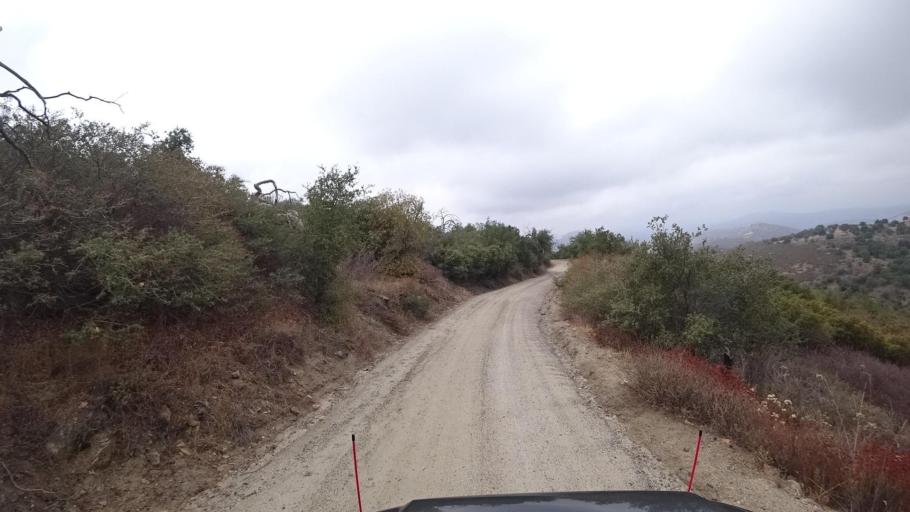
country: US
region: California
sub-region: San Diego County
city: Julian
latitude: 32.9922
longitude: -116.6552
